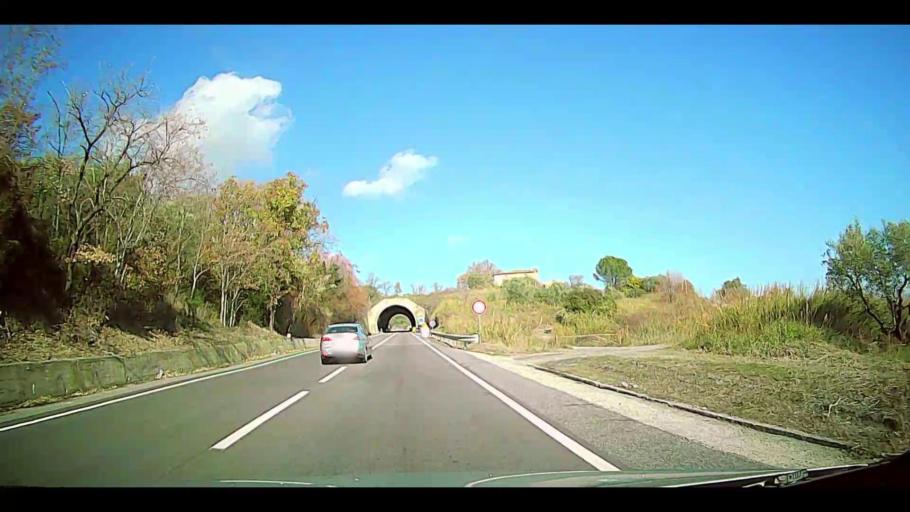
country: IT
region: Calabria
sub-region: Provincia di Crotone
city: Caccuri
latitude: 39.2181
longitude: 16.7958
